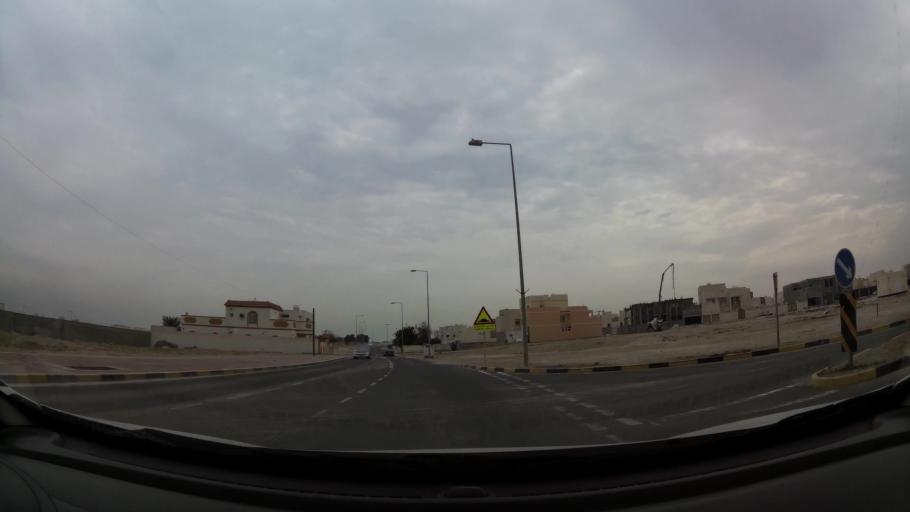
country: BH
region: Northern
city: Ar Rifa'
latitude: 26.0541
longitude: 50.6179
